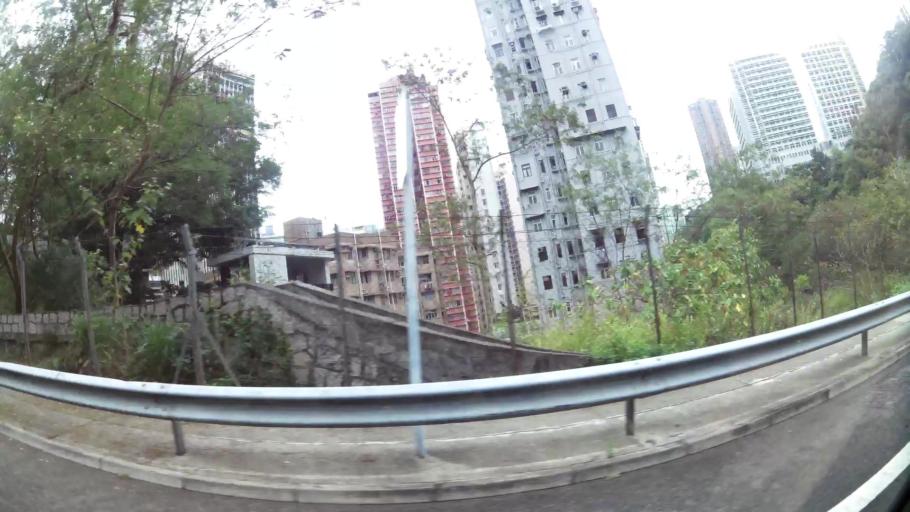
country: HK
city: Hong Kong
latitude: 22.2786
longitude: 114.1295
